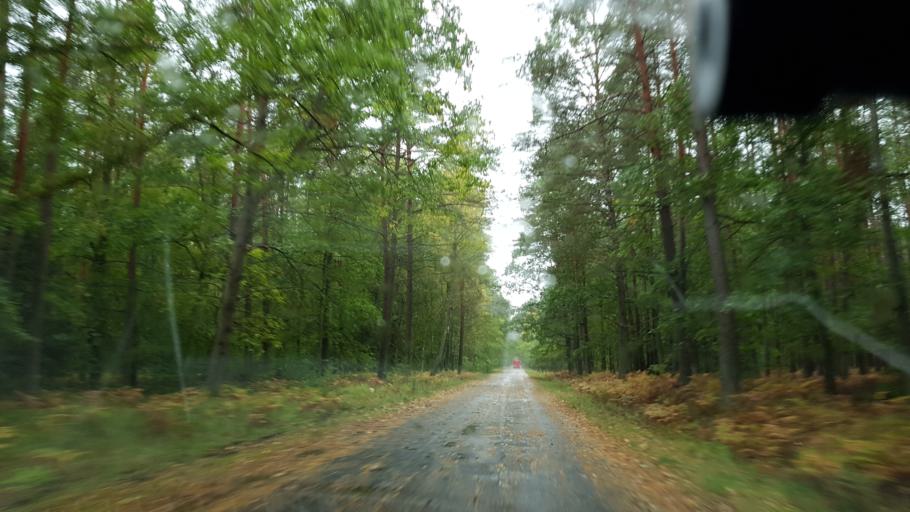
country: PL
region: West Pomeranian Voivodeship
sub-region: Powiat goleniowski
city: Przybiernow
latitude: 53.7084
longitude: 14.7463
